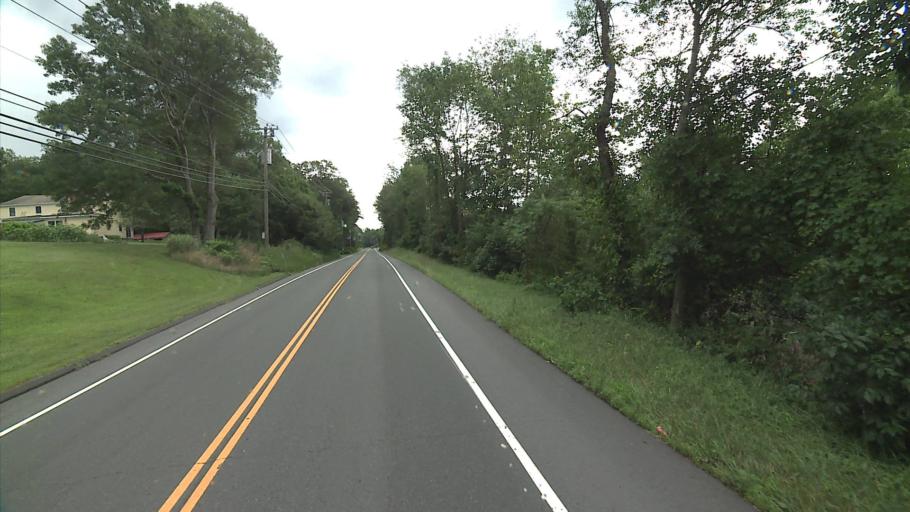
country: US
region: Connecticut
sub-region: New Haven County
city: Southbury
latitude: 41.4738
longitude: -73.1889
